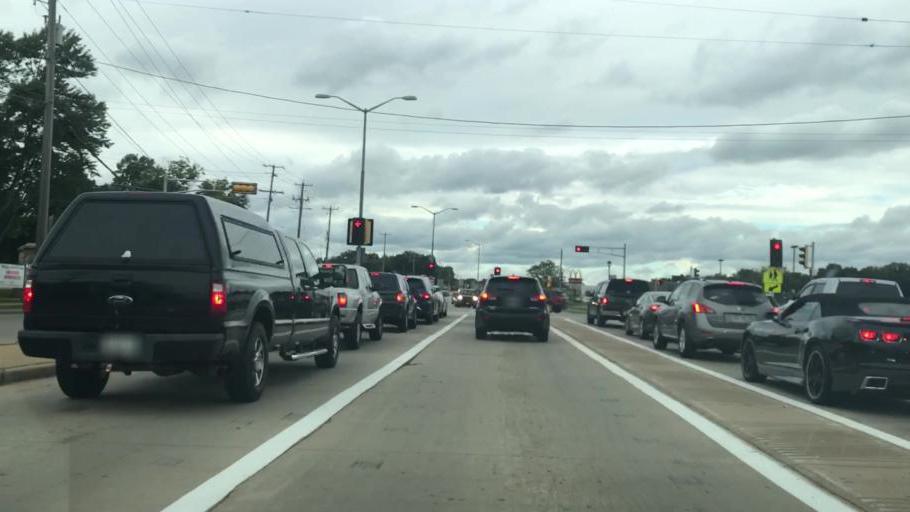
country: US
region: Wisconsin
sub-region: Waukesha County
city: Mukwonago
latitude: 42.8738
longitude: -88.3376
